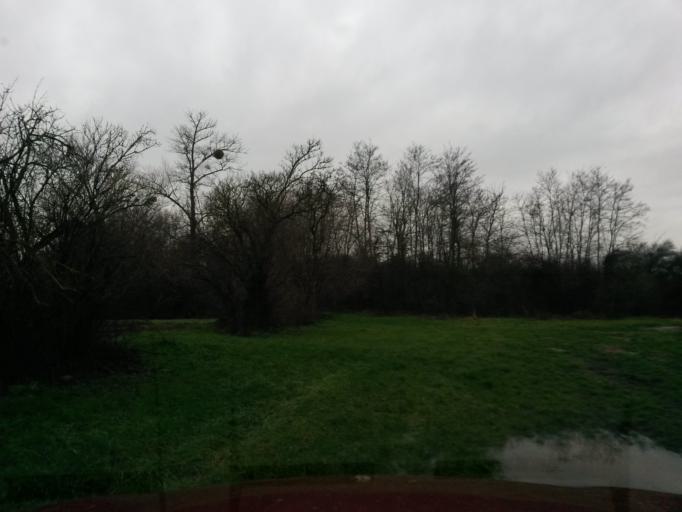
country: SK
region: Kosicky
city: Sobrance
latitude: 48.6423
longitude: 22.0802
